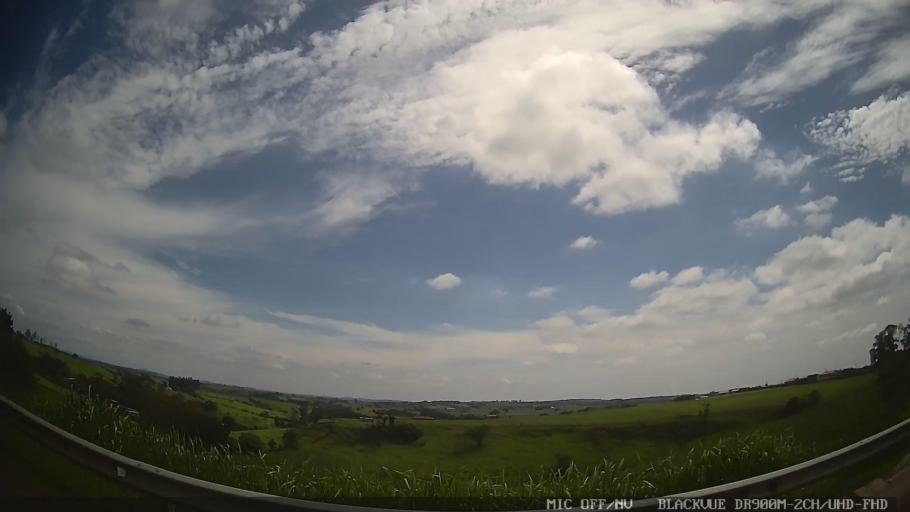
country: BR
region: Sao Paulo
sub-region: Laranjal Paulista
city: Laranjal Paulista
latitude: -23.0871
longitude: -47.7807
